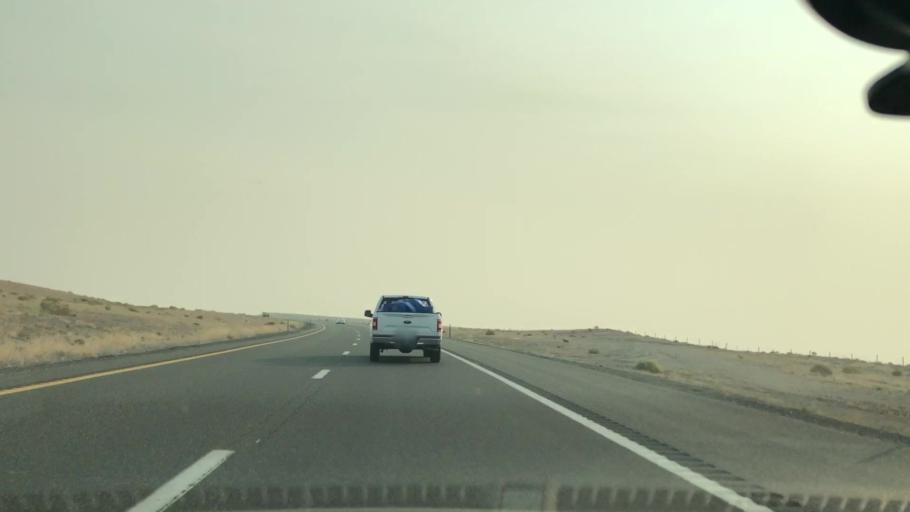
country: US
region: Nevada
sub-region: Pershing County
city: Lovelock
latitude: 39.9599
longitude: -118.7055
